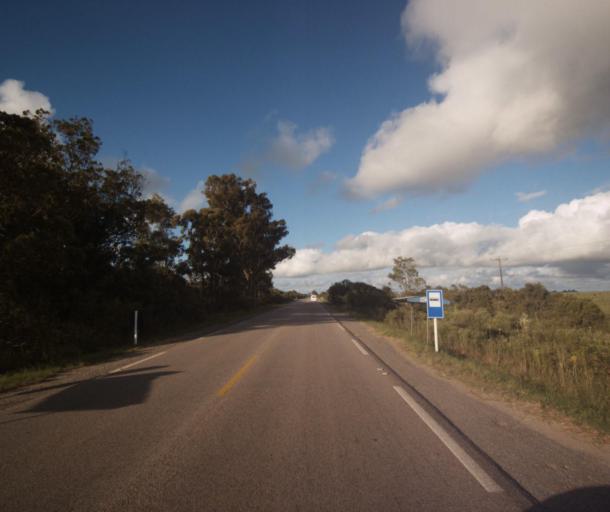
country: BR
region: Rio Grande do Sul
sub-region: Rio Grande
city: Rio Grande
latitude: -32.1852
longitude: -52.4278
